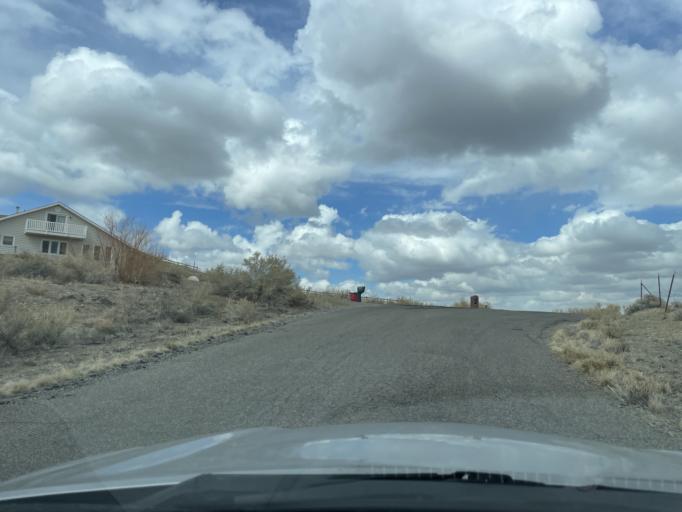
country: US
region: Colorado
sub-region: Mesa County
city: Redlands
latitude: 39.0578
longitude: -108.6020
